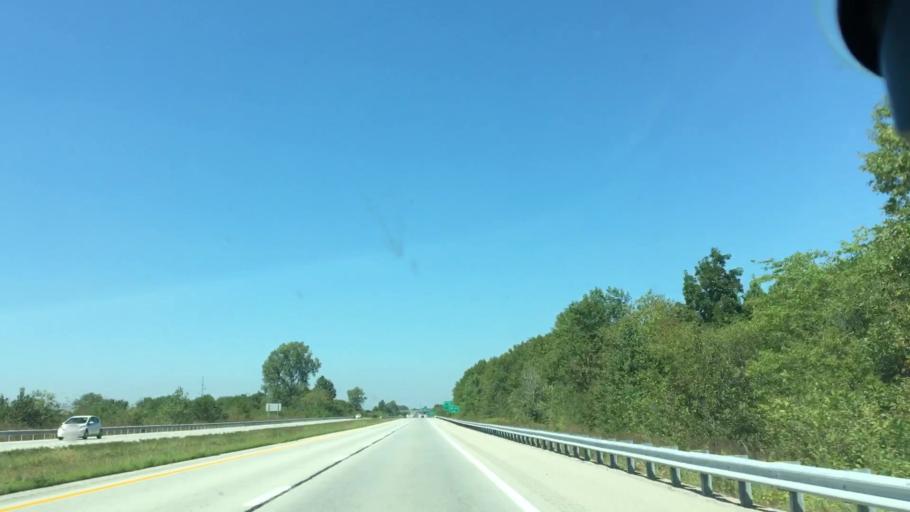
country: US
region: Kentucky
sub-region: Henderson County
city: Henderson
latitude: 37.7837
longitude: -87.5471
